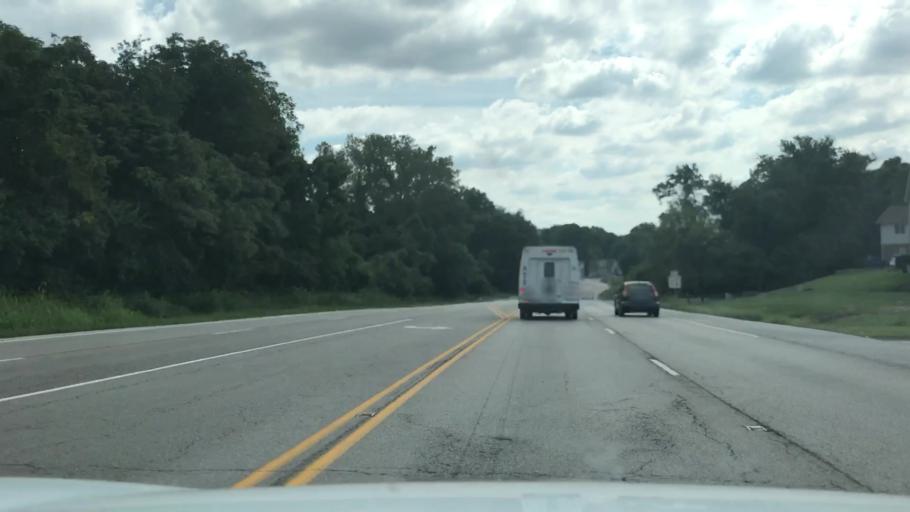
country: US
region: Illinois
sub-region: Saint Clair County
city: Swansea
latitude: 38.5443
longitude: -90.0504
